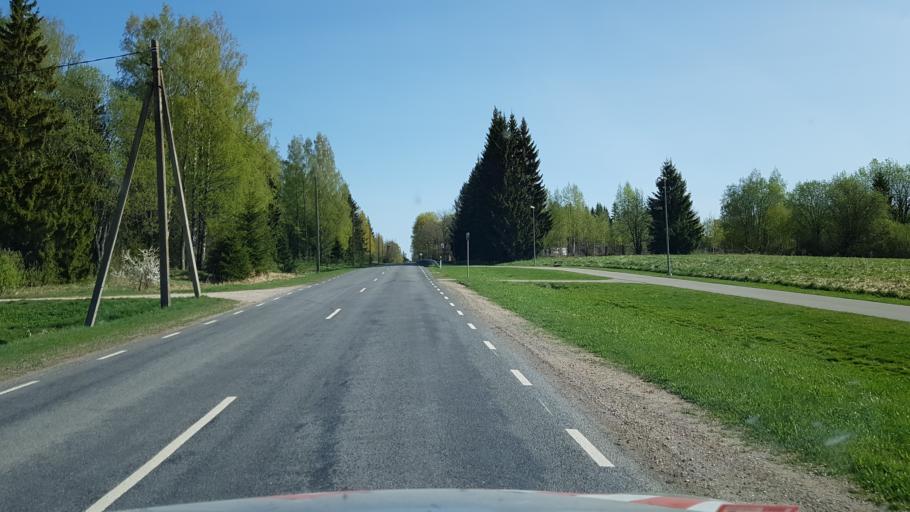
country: EE
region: Viljandimaa
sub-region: Abja vald
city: Abja-Paluoja
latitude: 58.1587
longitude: 25.4337
